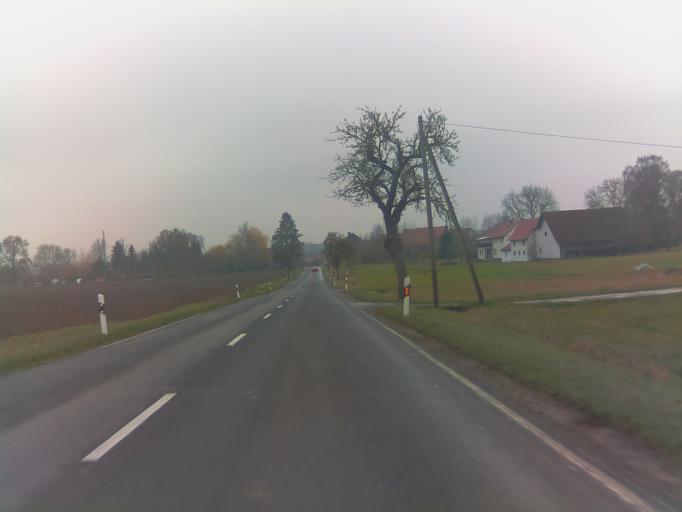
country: DE
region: Thuringia
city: Romhild
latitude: 50.4228
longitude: 10.5414
